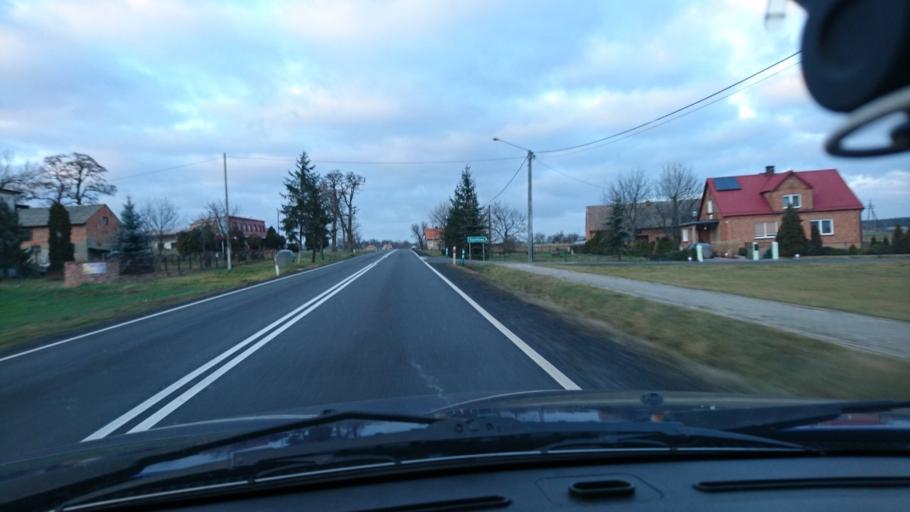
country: PL
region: Greater Poland Voivodeship
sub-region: Powiat ostrzeszowski
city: Ostrzeszow
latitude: 51.3583
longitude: 17.9467
